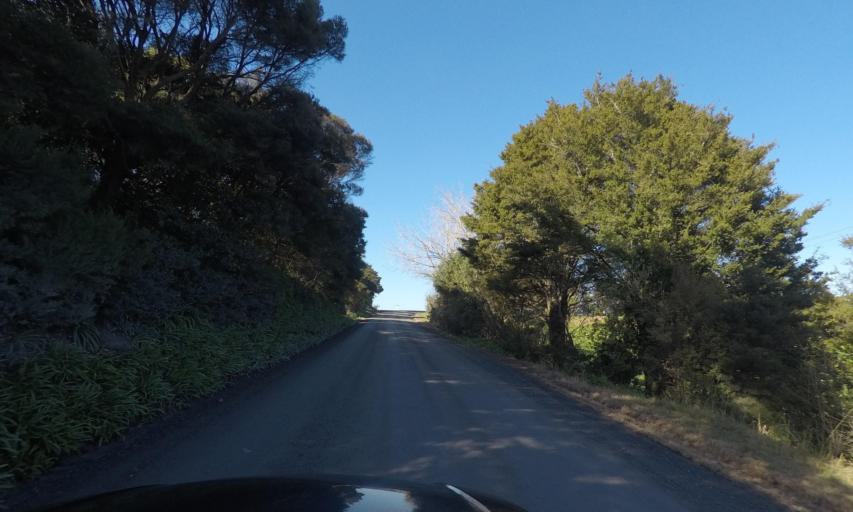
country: NZ
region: Auckland
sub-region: Auckland
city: Wellsford
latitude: -36.1609
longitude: 174.6034
